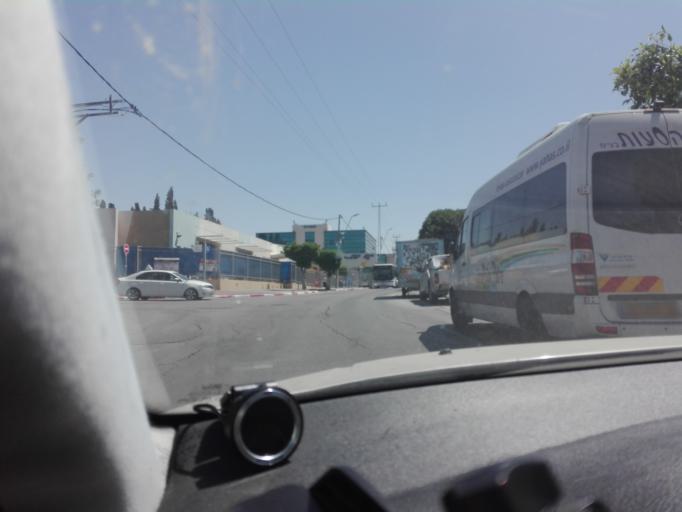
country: IL
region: Central District
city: Bene 'Ayish
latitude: 31.7321
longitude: 34.7474
